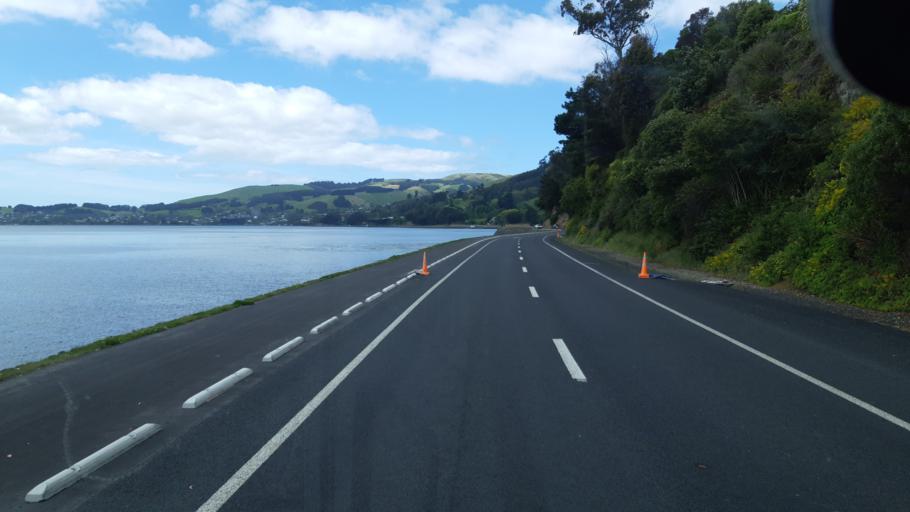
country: NZ
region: Otago
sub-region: Dunedin City
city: Dunedin
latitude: -45.8794
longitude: 170.5623
